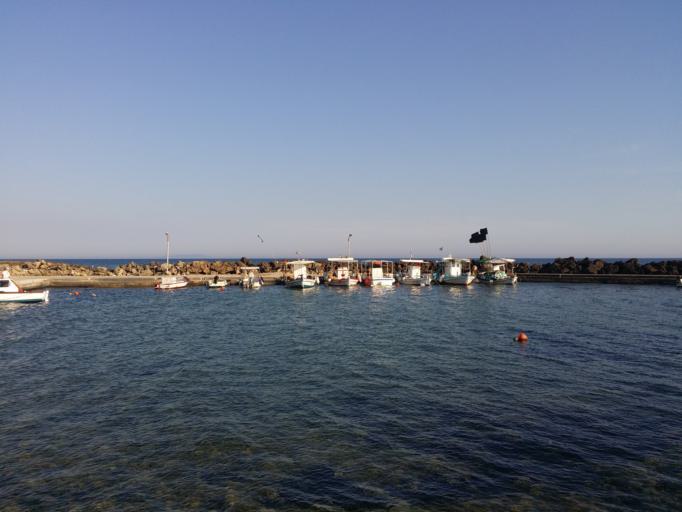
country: GR
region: Ionian Islands
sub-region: Nomos Kerkyras
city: Perivoli
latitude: 39.4264
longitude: 19.9437
